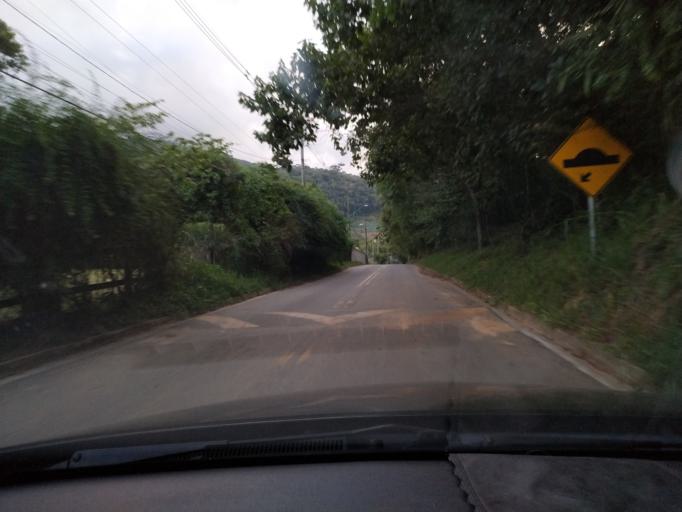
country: BR
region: Sao Paulo
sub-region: Campos Do Jordao
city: Campos do Jordao
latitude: -22.8083
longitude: -45.6454
